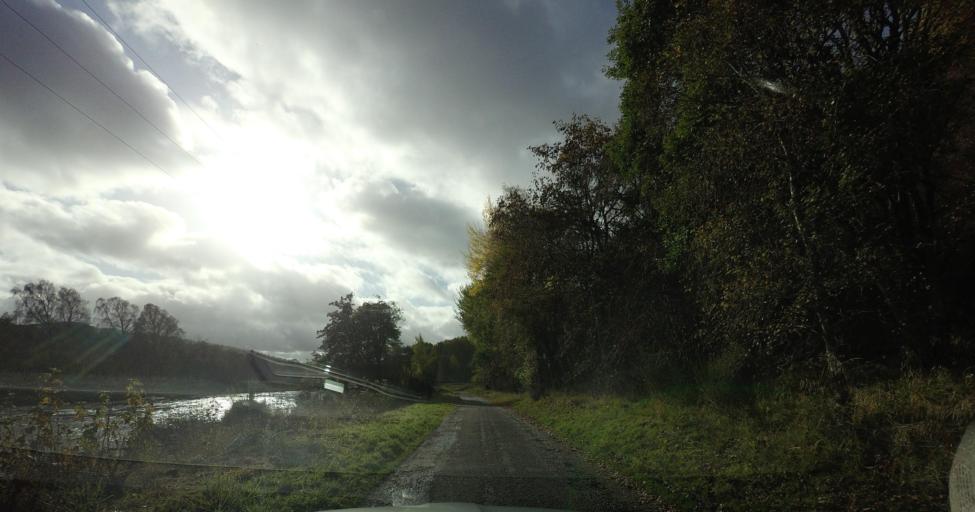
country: GB
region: Scotland
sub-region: Highland
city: Grantown on Spey
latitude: 57.3178
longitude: -3.6155
